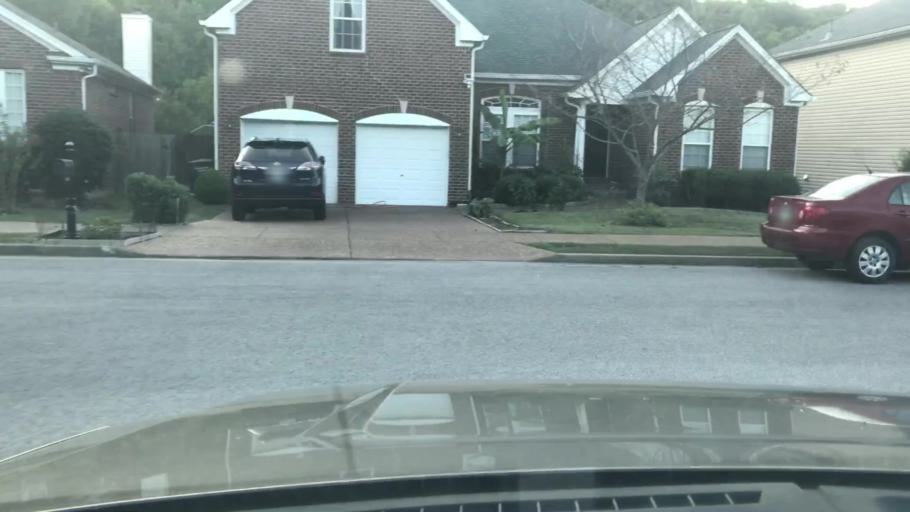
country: US
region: Tennessee
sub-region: Davidson County
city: Belle Meade
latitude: 36.1148
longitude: -86.9327
